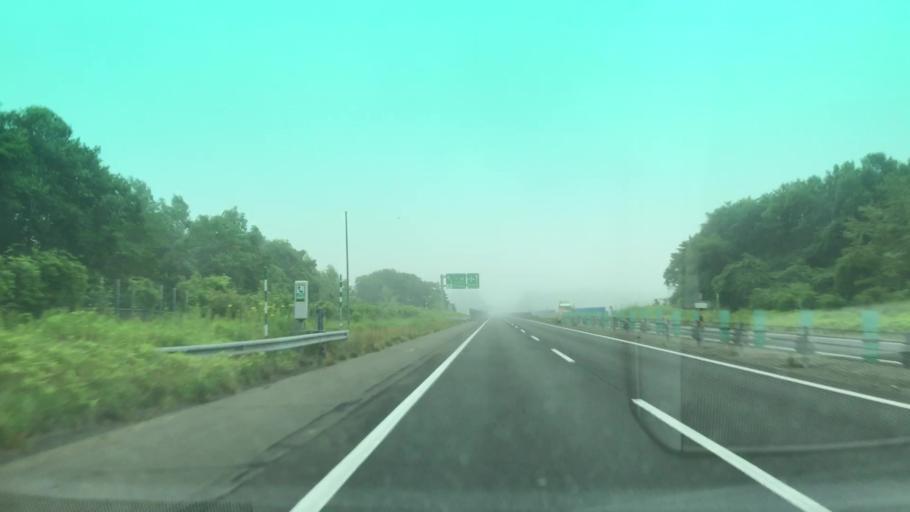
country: JP
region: Hokkaido
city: Chitose
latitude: 42.8211
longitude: 141.6172
